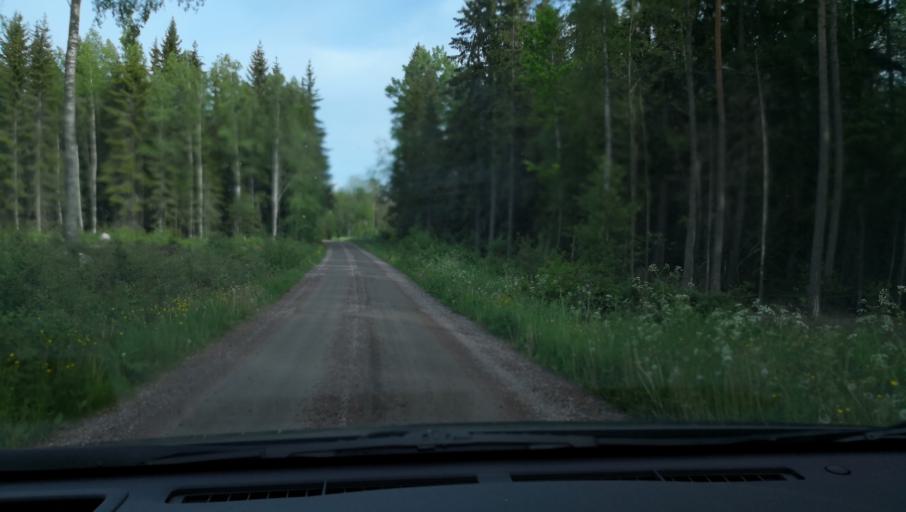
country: SE
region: Vaestmanland
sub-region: Kungsors Kommun
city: Kungsoer
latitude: 59.3586
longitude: 16.0563
